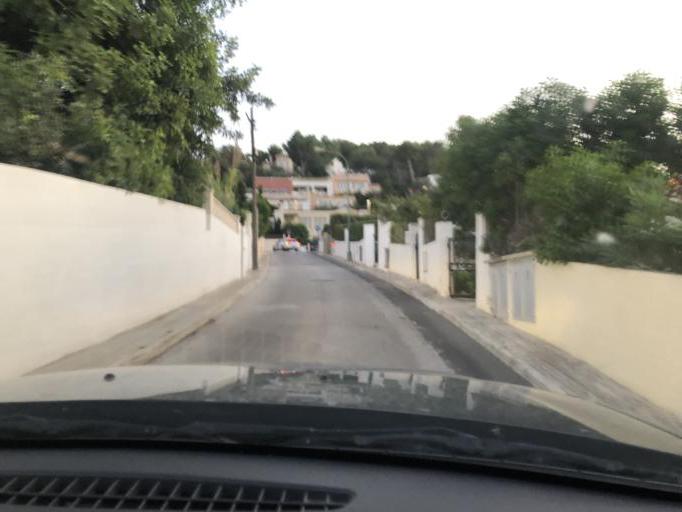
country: ES
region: Balearic Islands
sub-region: Illes Balears
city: Santa Ponsa
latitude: 39.5247
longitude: 2.4823
